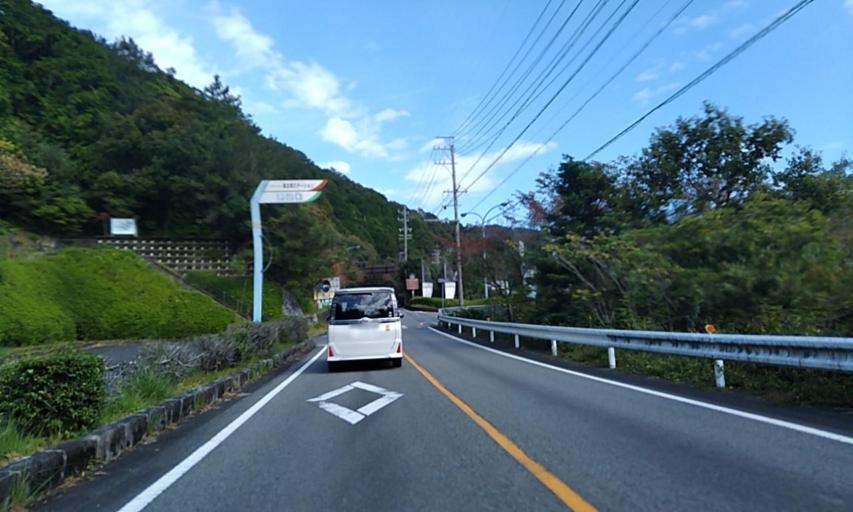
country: JP
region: Mie
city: Owase
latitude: 34.2094
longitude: 136.3542
